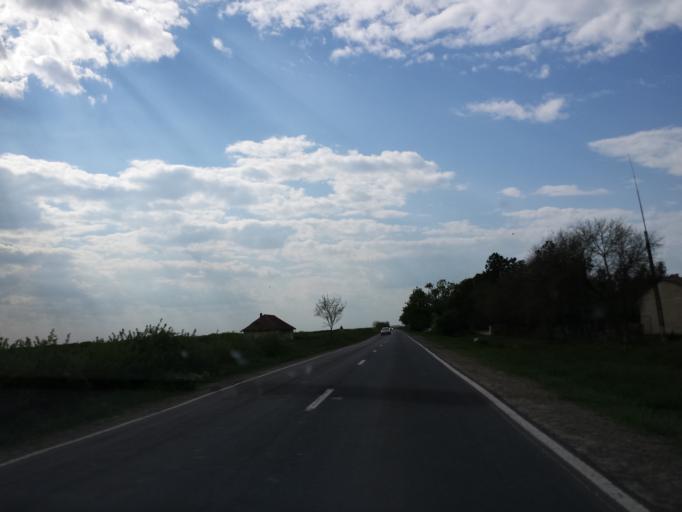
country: RO
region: Timis
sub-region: Comuna Cenad
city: Cenad
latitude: 46.1306
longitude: 20.5121
